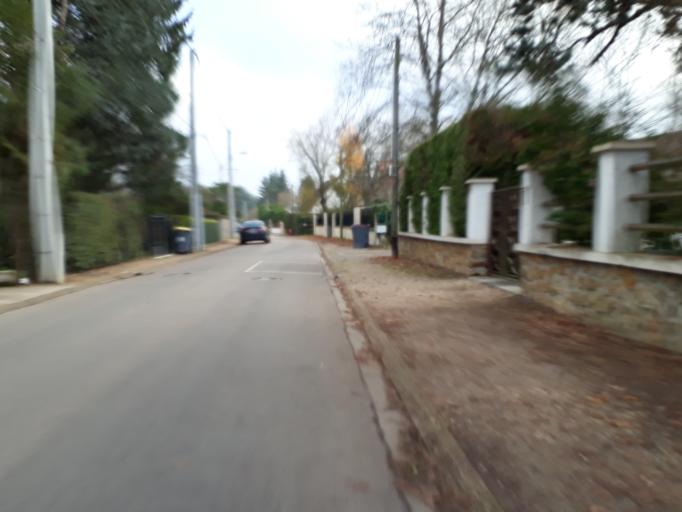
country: FR
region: Ile-de-France
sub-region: Departement de Seine-et-Marne
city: Bois-le-Roi
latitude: 48.4706
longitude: 2.6940
